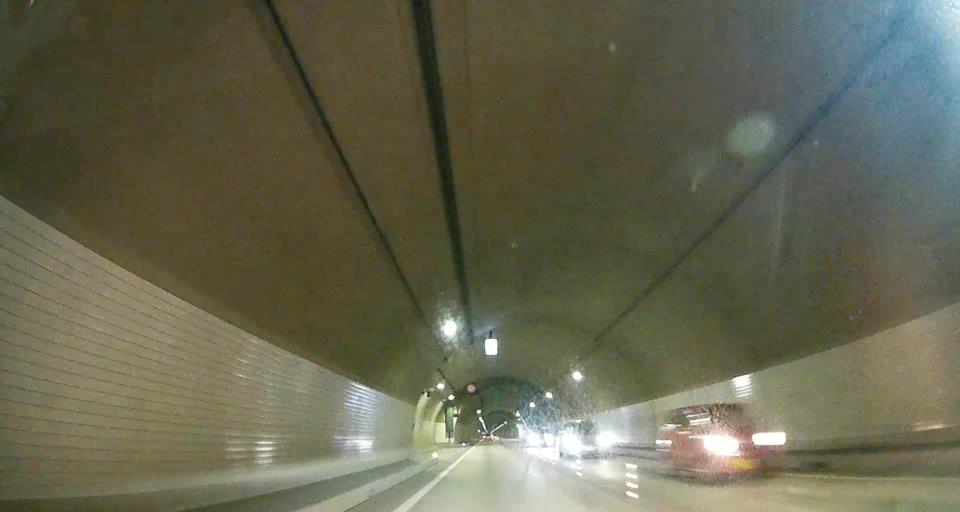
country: JP
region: Iwate
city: Miyako
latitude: 39.9289
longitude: 141.8718
